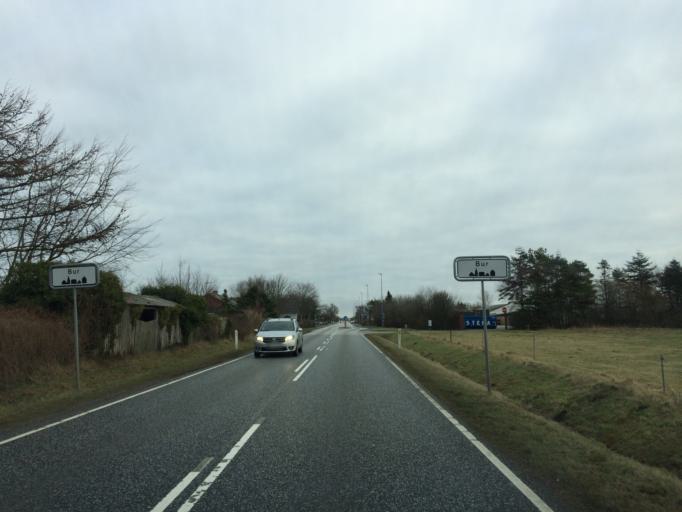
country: DK
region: Central Jutland
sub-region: Holstebro Kommune
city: Ulfborg
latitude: 56.3659
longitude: 8.4258
